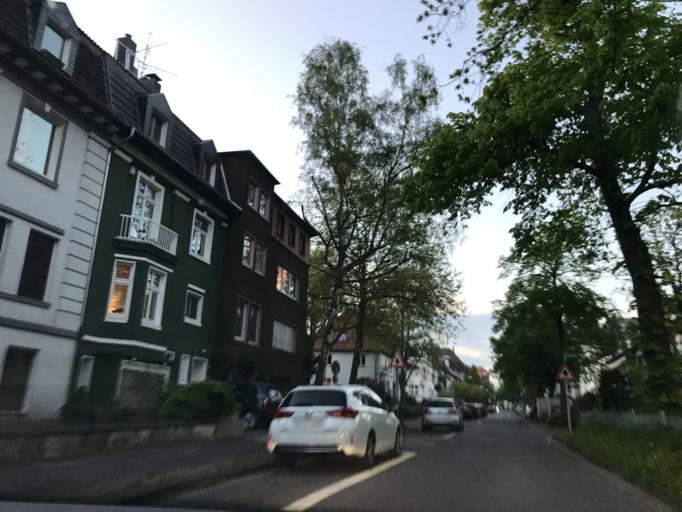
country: DE
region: North Rhine-Westphalia
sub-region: Regierungsbezirk Dusseldorf
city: Essen
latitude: 51.4345
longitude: 6.9956
